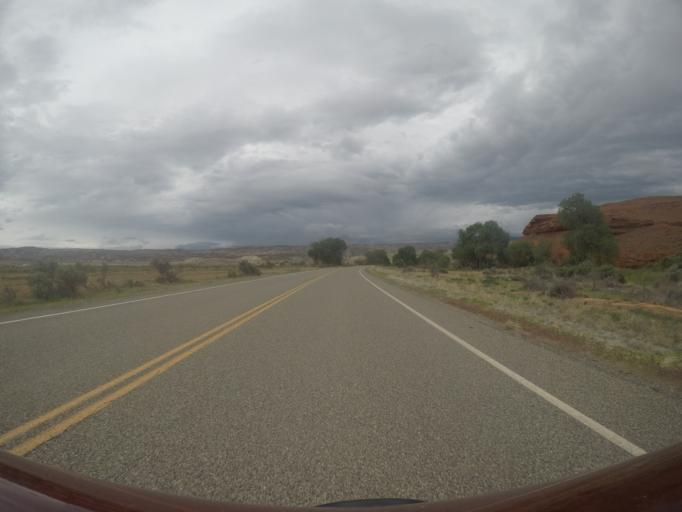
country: US
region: Wyoming
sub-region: Big Horn County
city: Lovell
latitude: 44.9639
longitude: -108.2805
